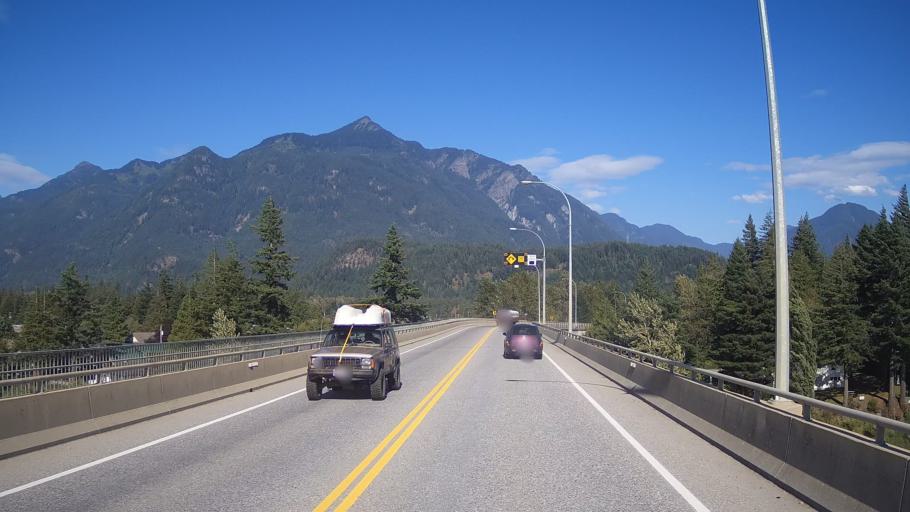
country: CA
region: British Columbia
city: Hope
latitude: 49.3863
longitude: -121.4521
